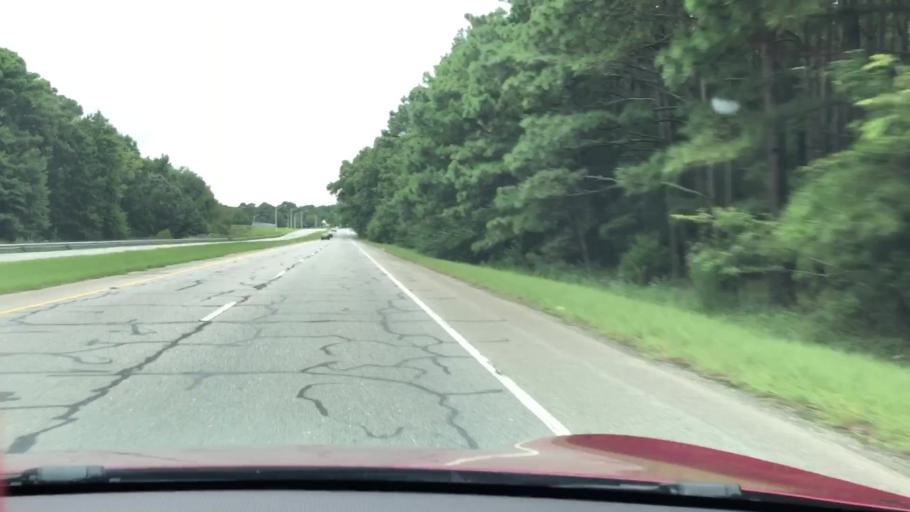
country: US
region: Virginia
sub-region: City of Virginia Beach
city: Virginia Beach
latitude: 36.8326
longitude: -76.0117
